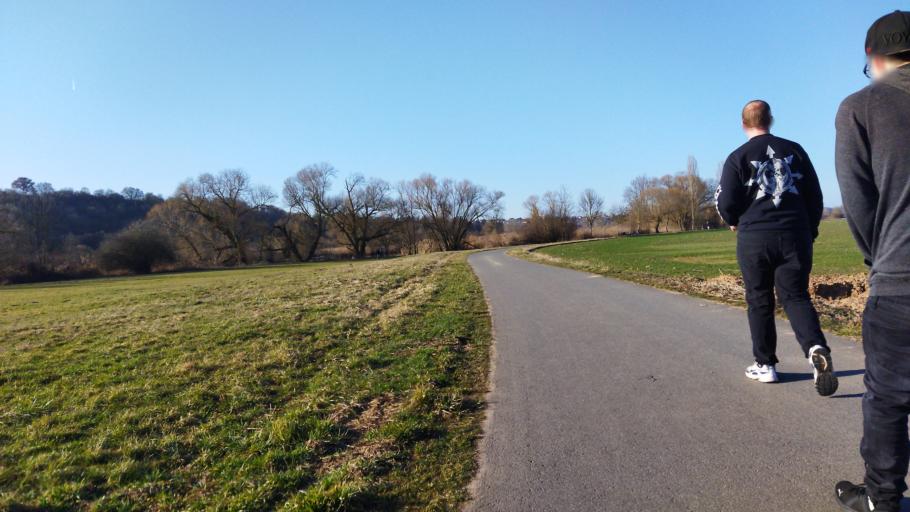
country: DE
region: Bavaria
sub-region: Regierungsbezirk Unterfranken
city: Kitzingen
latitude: 49.7516
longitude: 10.1605
